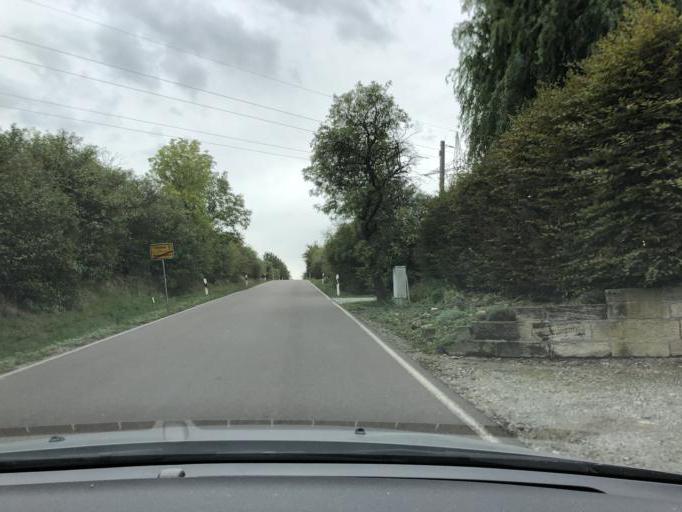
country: DE
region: Saxony-Anhalt
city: Bad Kosen
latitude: 51.1543
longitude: 11.7064
